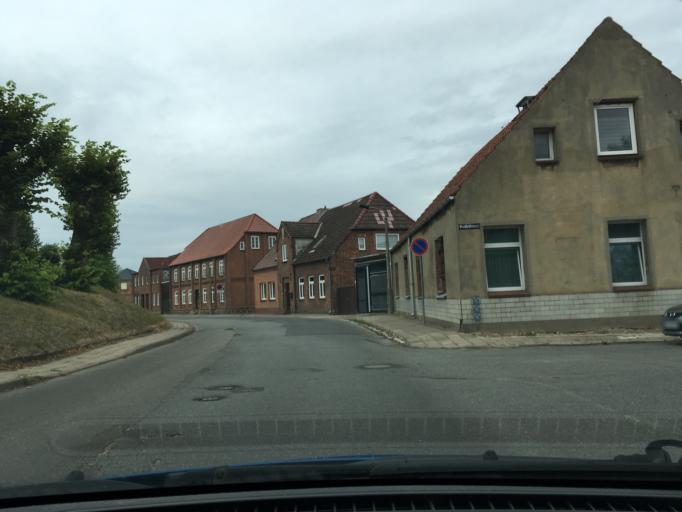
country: DE
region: Mecklenburg-Vorpommern
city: Wittenburg
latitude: 53.5115
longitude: 11.0771
